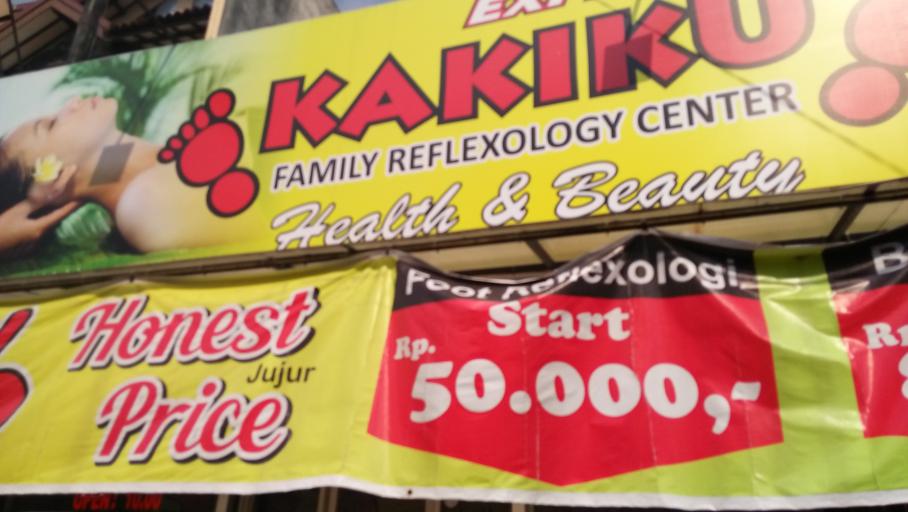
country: ID
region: Daerah Istimewa Yogyakarta
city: Yogyakarta
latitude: -7.7911
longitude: 110.3618
